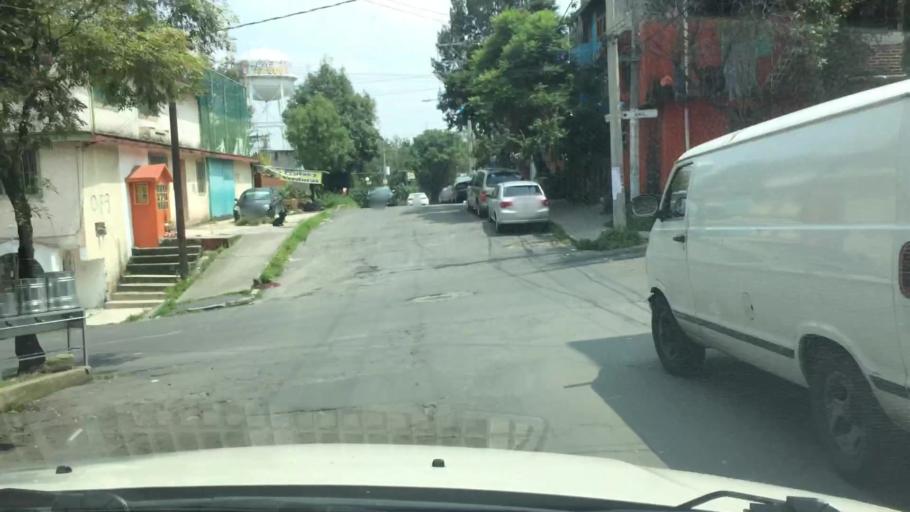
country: MX
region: Mexico City
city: Magdalena Contreras
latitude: 19.2975
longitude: -99.2231
